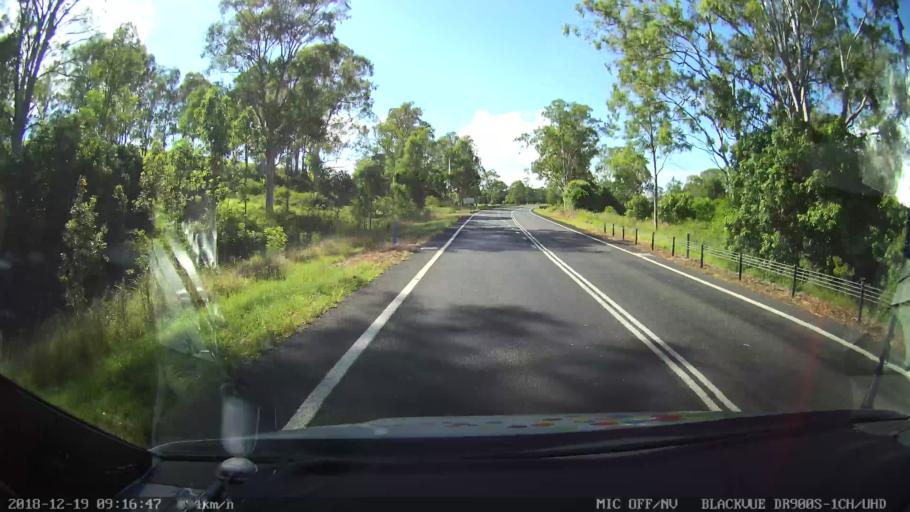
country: AU
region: New South Wales
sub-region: Kyogle
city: Kyogle
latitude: -28.5249
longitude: 152.9704
